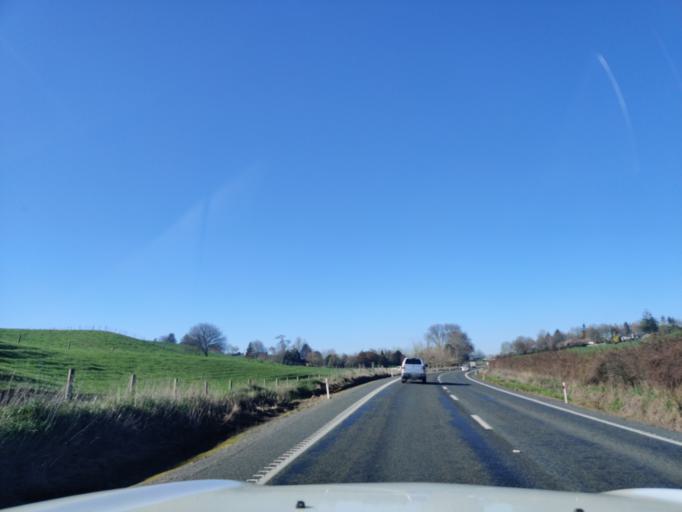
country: NZ
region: Waikato
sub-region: Matamata-Piako District
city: Matamata
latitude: -38.0075
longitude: 175.7710
